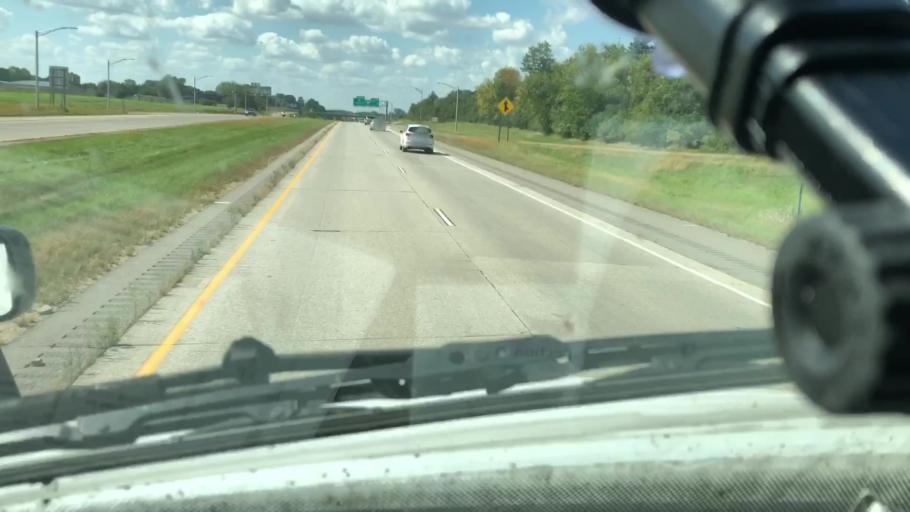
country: US
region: Minnesota
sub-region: Mower County
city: Austin
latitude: 43.6744
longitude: -92.9309
